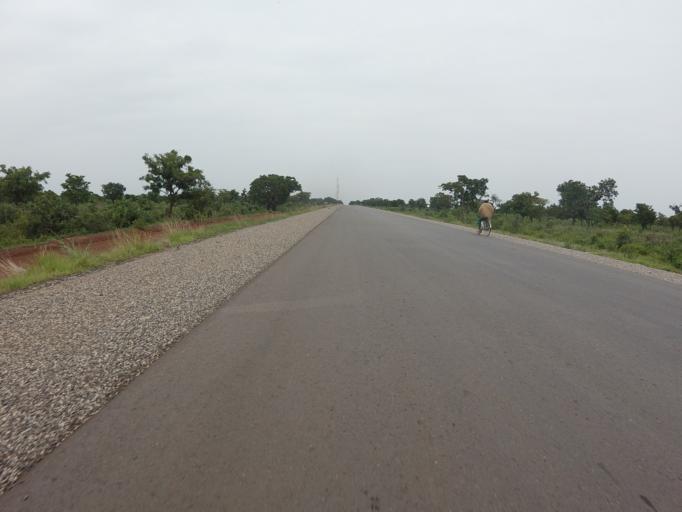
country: GH
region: Northern
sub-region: Yendi
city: Yendi
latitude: 9.2915
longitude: 0.0180
